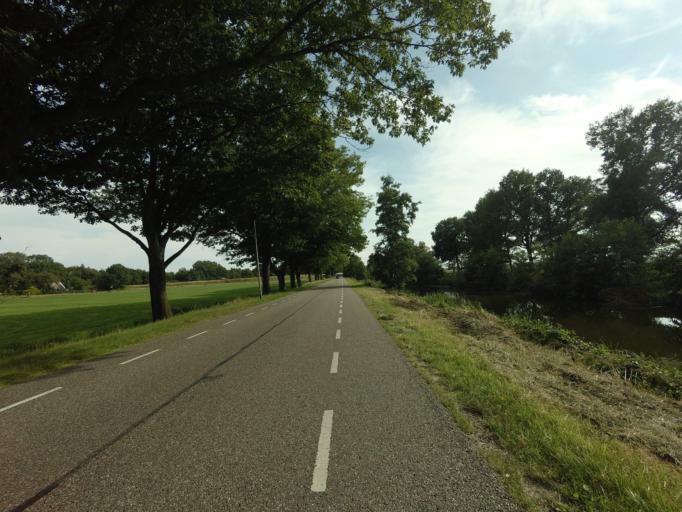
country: NL
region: Drenthe
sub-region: Gemeente Coevorden
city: Coevorden
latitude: 52.6731
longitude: 6.7226
